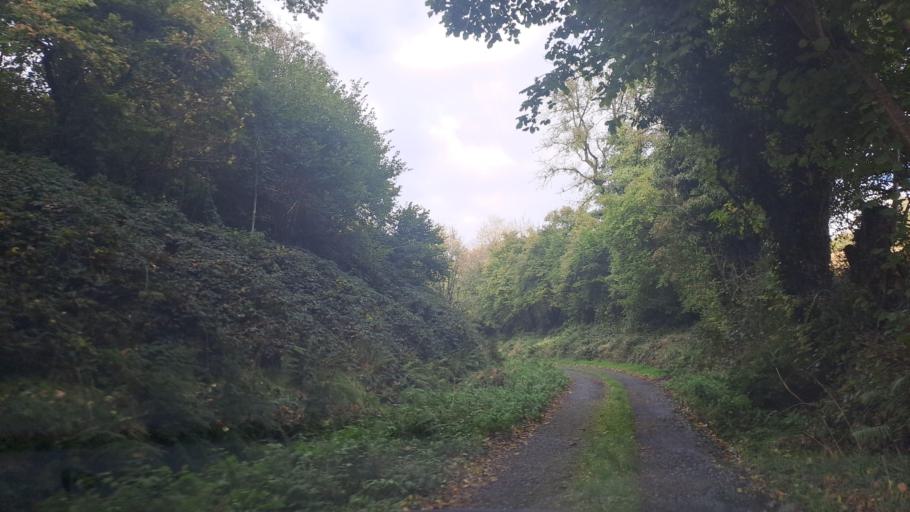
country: IE
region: Ulster
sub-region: An Cabhan
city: Kingscourt
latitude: 54.0019
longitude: -6.8172
